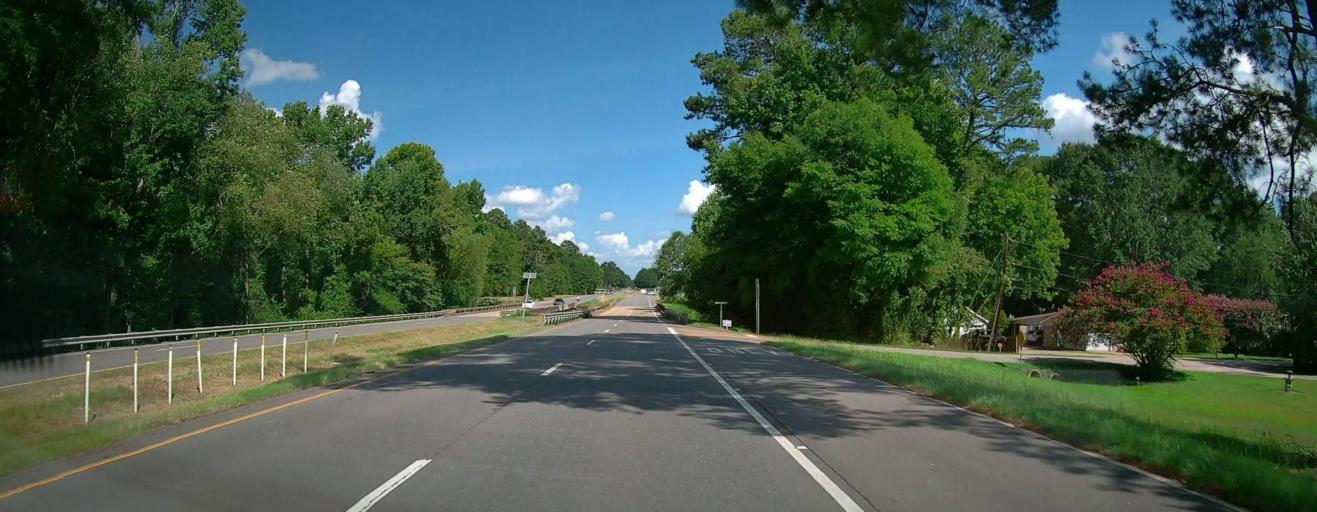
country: US
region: Alabama
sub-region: Tuscaloosa County
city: Northport
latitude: 33.2478
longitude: -87.6781
